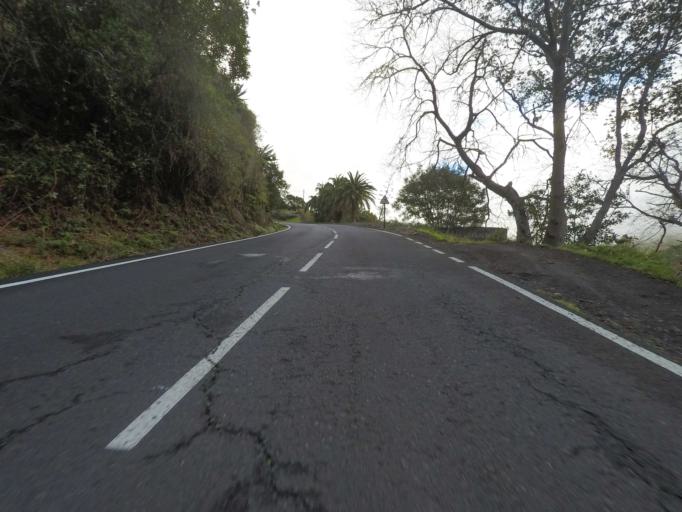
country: ES
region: Canary Islands
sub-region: Provincia de Santa Cruz de Tenerife
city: Hermigua
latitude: 28.1297
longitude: -17.2108
